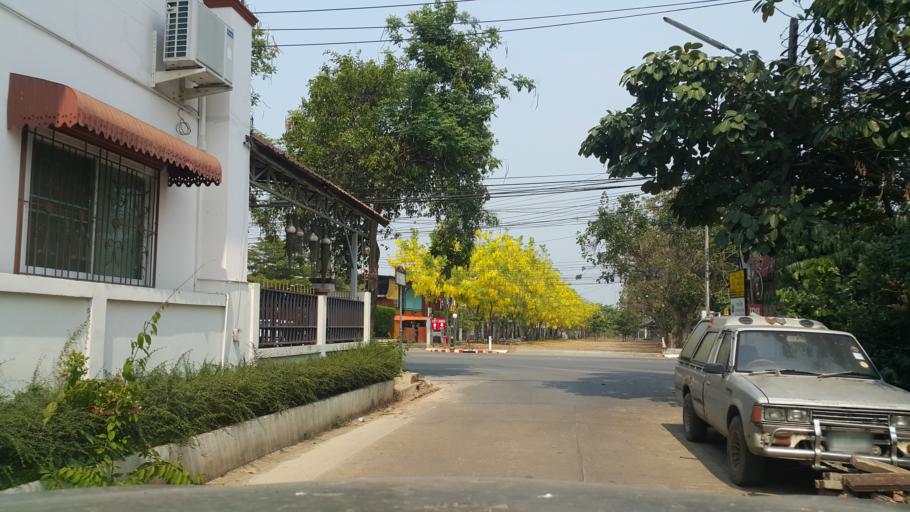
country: TH
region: Chiang Mai
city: Chiang Mai
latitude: 18.7874
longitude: 98.9622
